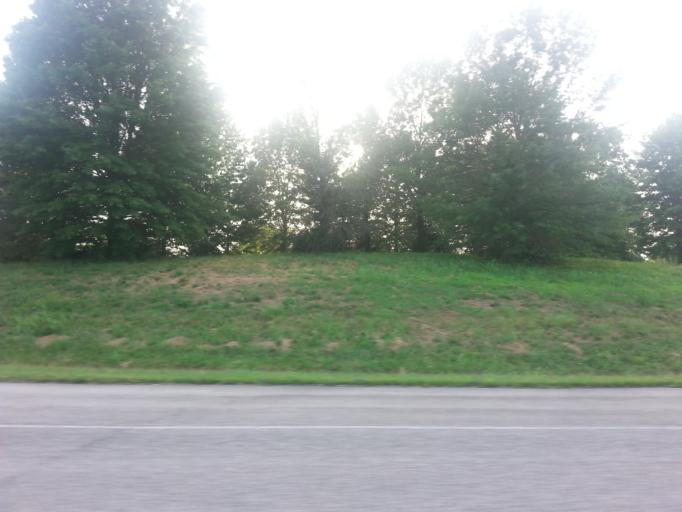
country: US
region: Tennessee
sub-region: Knox County
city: Farragut
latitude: 35.9487
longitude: -84.1557
